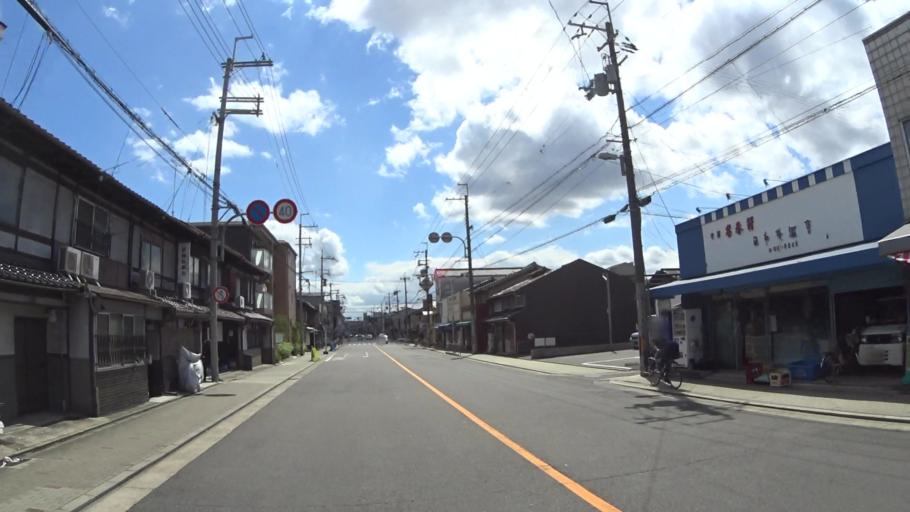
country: JP
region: Kyoto
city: Kyoto
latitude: 34.9771
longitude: 135.7619
